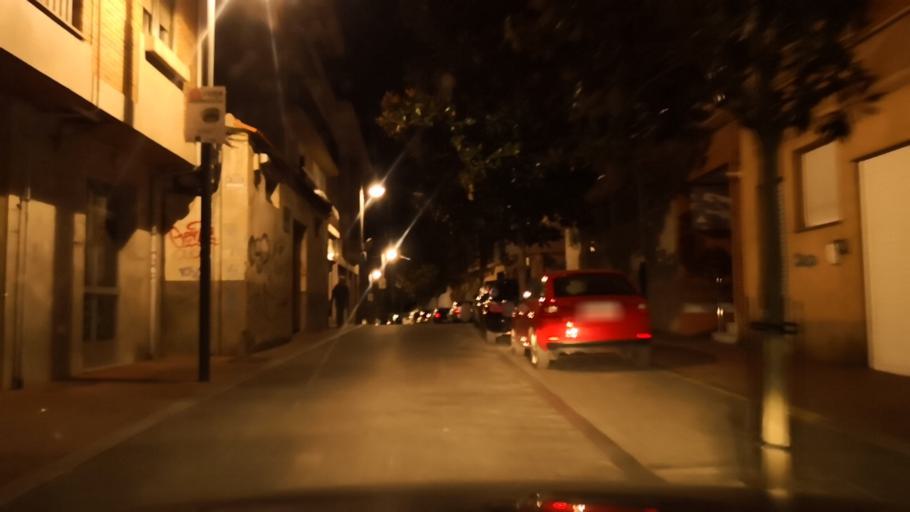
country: ES
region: Castille and Leon
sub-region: Provincia de Zamora
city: Benavente
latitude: 42.0021
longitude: -5.6783
